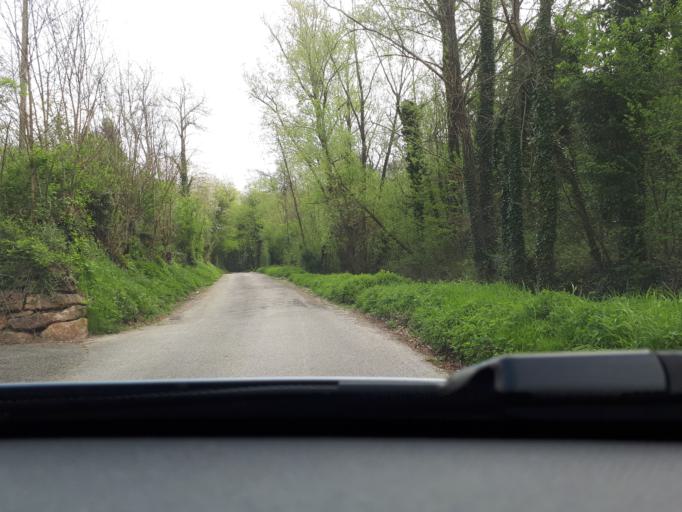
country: FR
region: Rhone-Alpes
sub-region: Departement de l'Isere
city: Bourgoin-Jallieu
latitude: 45.6068
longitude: 5.2745
